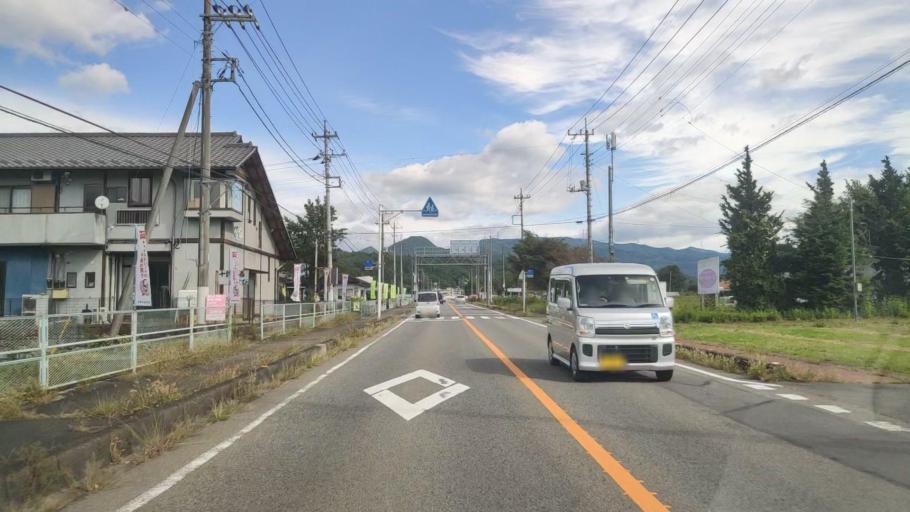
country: JP
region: Gunma
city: Nakanojomachi
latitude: 36.5955
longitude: 138.8624
